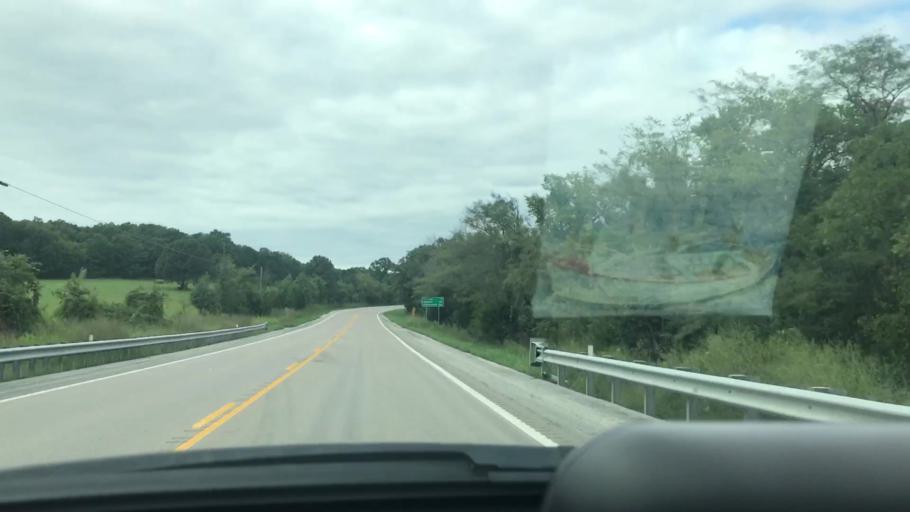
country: US
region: Missouri
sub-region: Benton County
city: Warsaw
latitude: 38.1234
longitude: -93.2791
